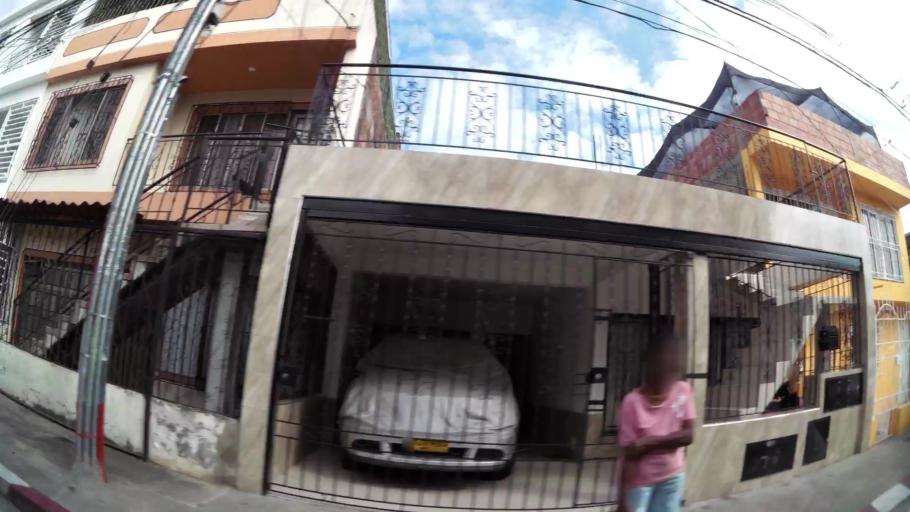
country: CO
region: Valle del Cauca
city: Cali
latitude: 3.4800
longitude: -76.4900
